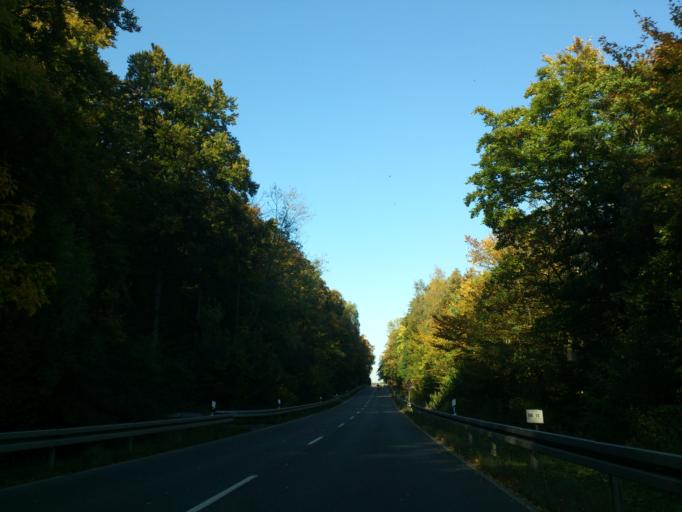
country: DE
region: Hesse
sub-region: Regierungsbezirk Kassel
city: Vellmar
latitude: 51.3442
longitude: 9.4158
